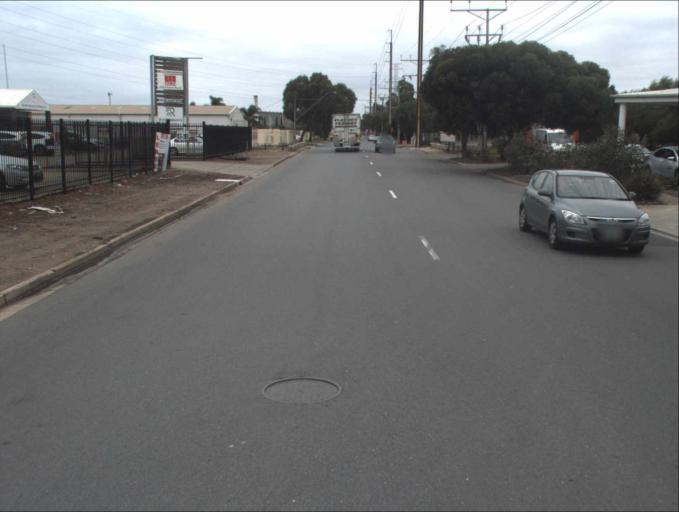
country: AU
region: South Australia
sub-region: Port Adelaide Enfield
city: Blair Athol
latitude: -34.8456
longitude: 138.5822
